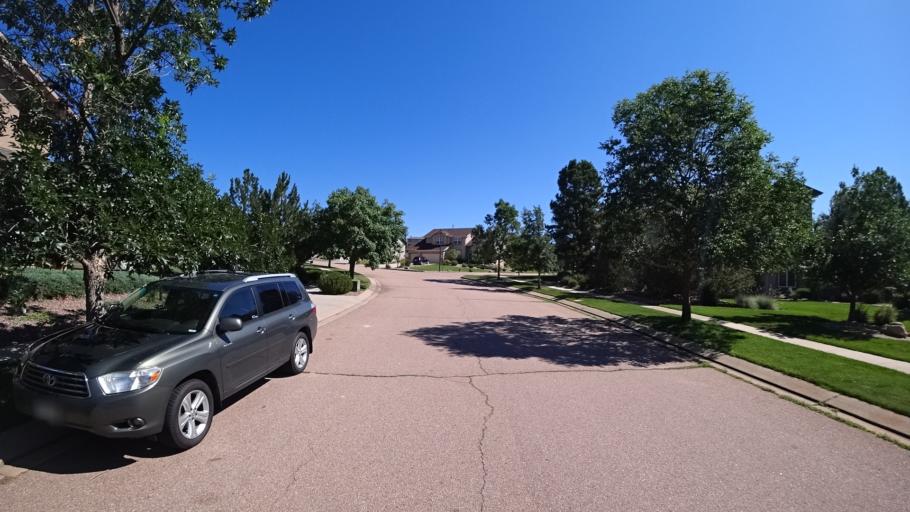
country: US
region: Colorado
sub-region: El Paso County
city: Gleneagle
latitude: 38.9718
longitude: -104.7794
